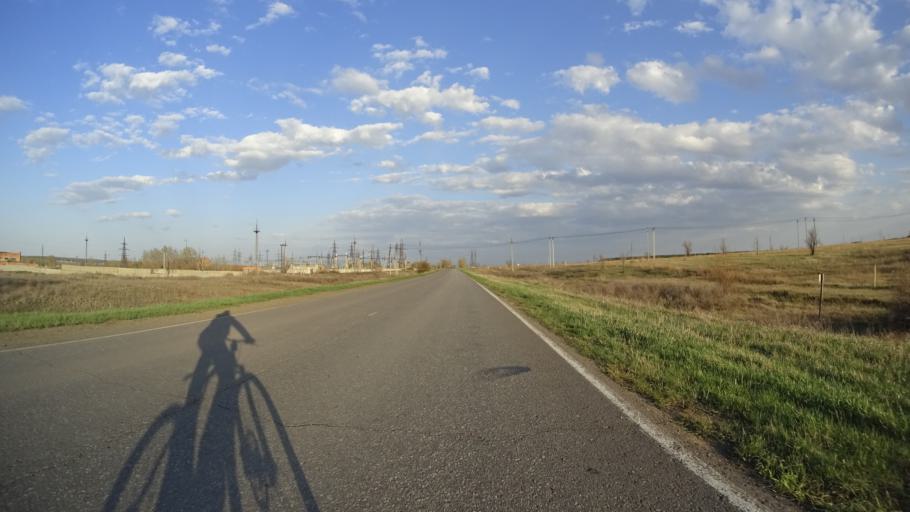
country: RU
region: Chelyabinsk
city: Troitsk
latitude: 54.0599
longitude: 61.5790
